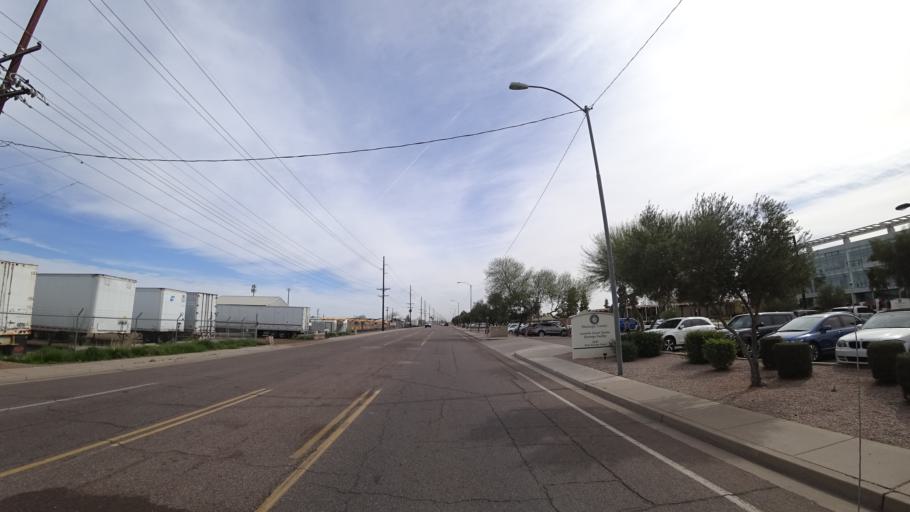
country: US
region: Arizona
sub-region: Maricopa County
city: Phoenix
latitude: 33.4296
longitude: -112.1293
